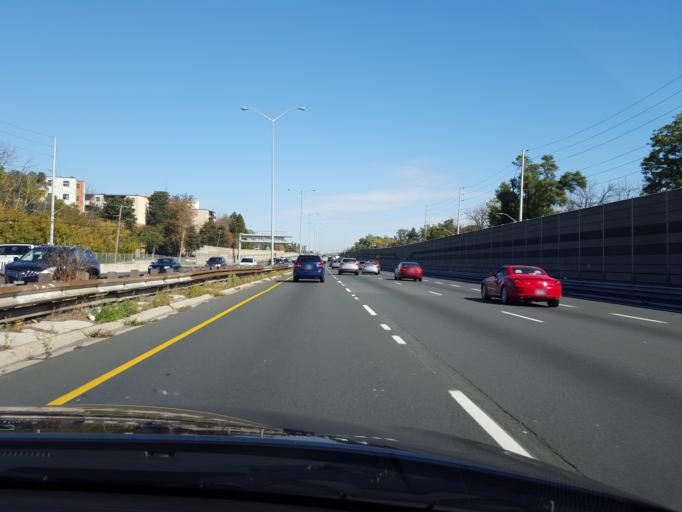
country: CA
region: Ontario
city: Mississauga
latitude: 43.5728
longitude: -79.5948
